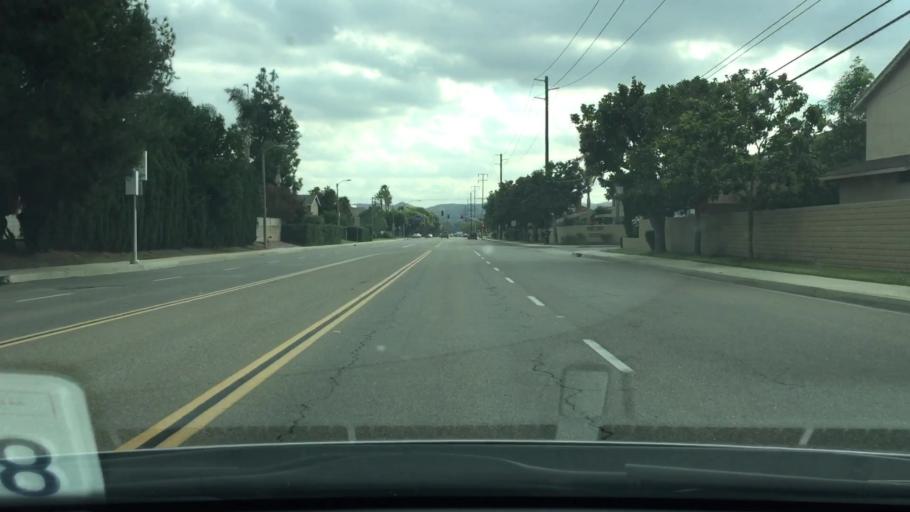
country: US
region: California
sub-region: San Bernardino County
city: Chino
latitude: 34.0067
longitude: -117.7154
